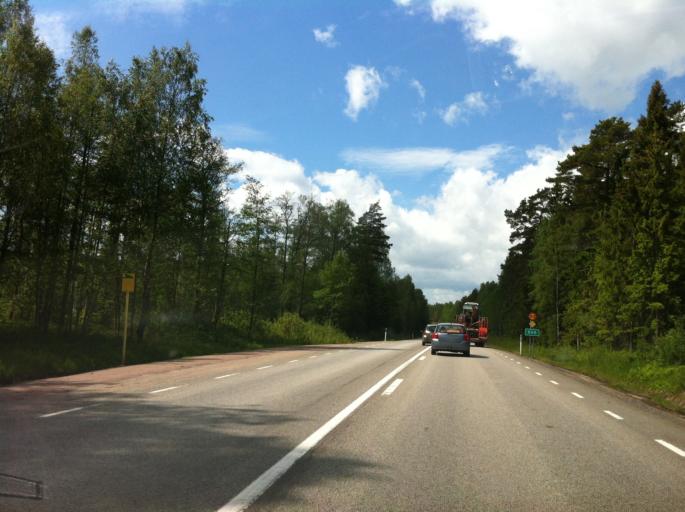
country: SE
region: Vaermland
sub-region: Saffle Kommun
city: Saeffle
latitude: 59.1508
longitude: 12.9598
